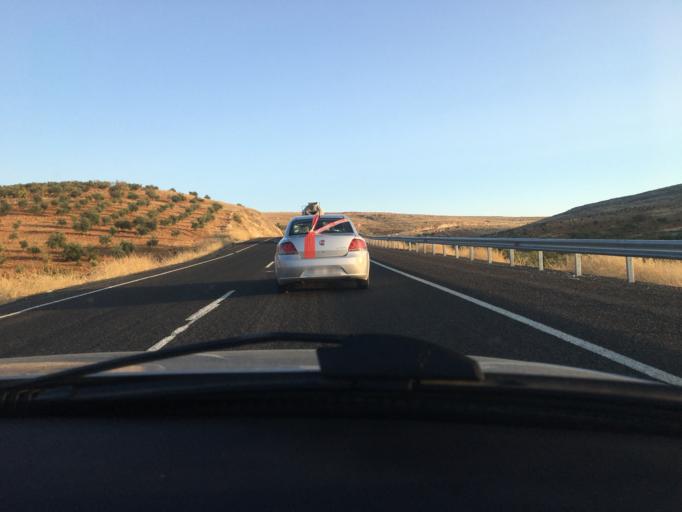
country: TR
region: Sanliurfa
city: Bogurtlen
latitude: 37.1890
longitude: 37.9716
